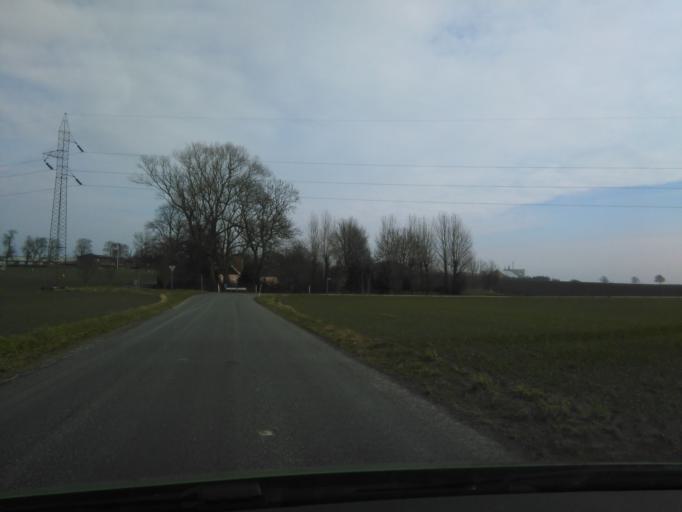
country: DK
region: Central Jutland
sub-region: Odder Kommune
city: Odder
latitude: 55.9408
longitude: 10.2077
